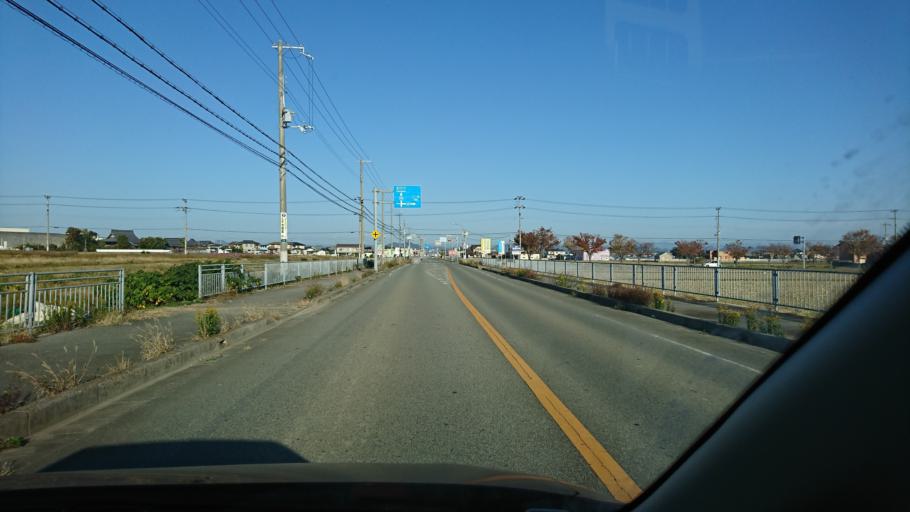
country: JP
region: Hyogo
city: Kakogawacho-honmachi
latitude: 34.7434
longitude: 134.9003
